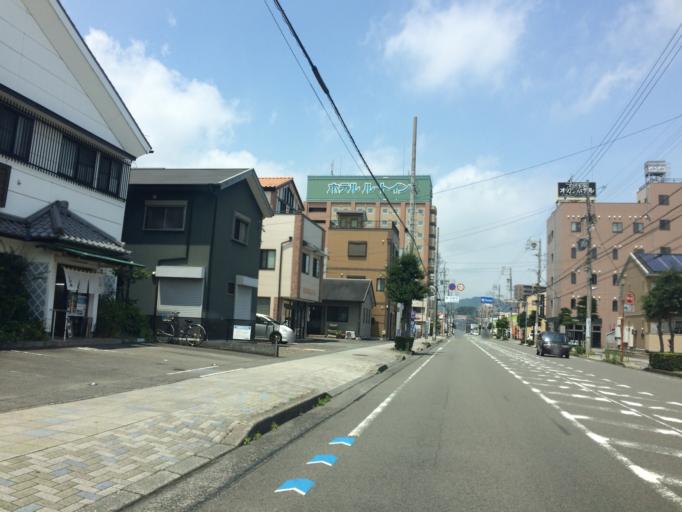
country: JP
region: Shizuoka
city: Fujieda
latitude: 34.8531
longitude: 138.2506
